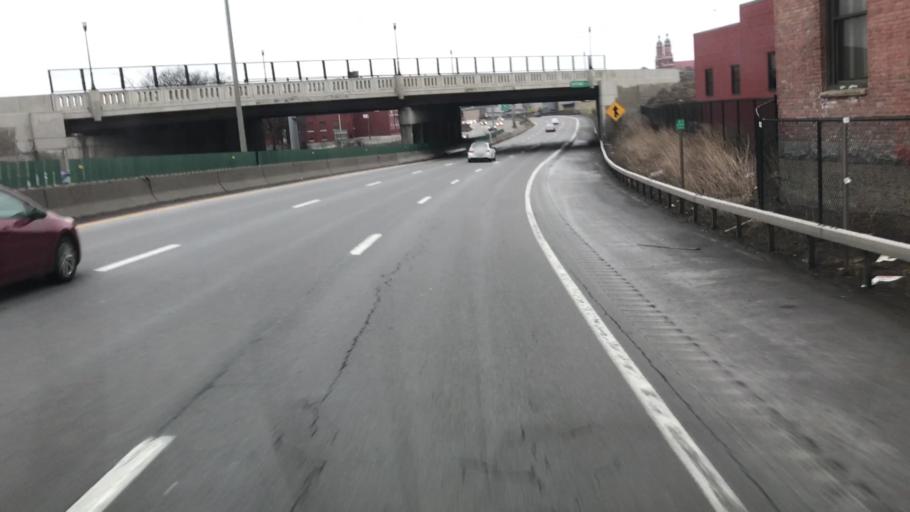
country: US
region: New York
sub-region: Onondaga County
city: Syracuse
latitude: 43.0558
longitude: -76.1532
